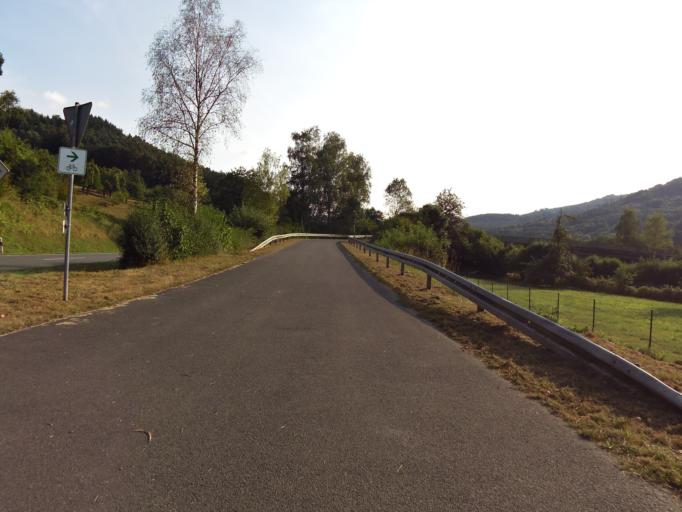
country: DE
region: Bavaria
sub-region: Regierungsbezirk Unterfranken
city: Weilbach
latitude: 49.6613
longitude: 9.2127
